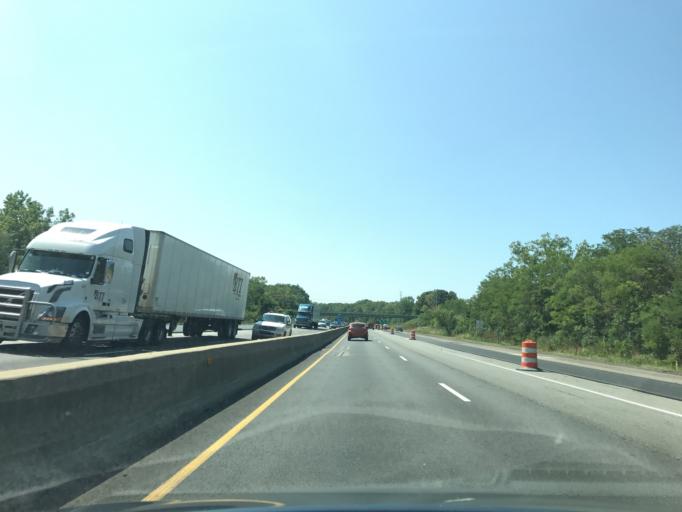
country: US
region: Indiana
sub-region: Porter County
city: Porter
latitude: 41.6241
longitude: -87.0638
